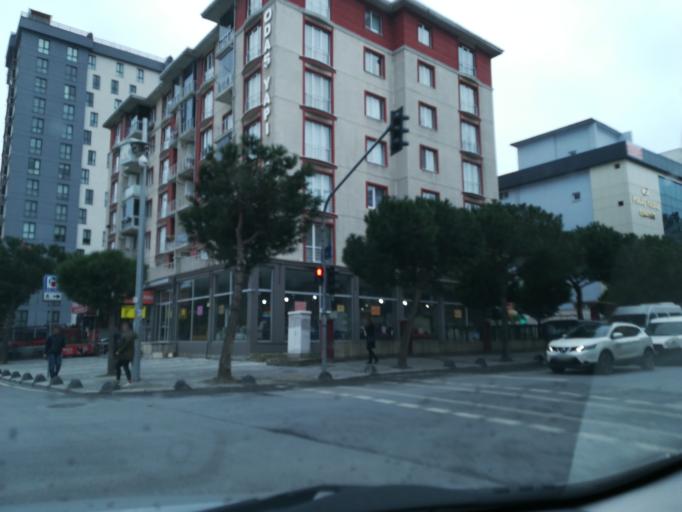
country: TR
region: Istanbul
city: Bagcilar
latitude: 41.0392
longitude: 28.8405
